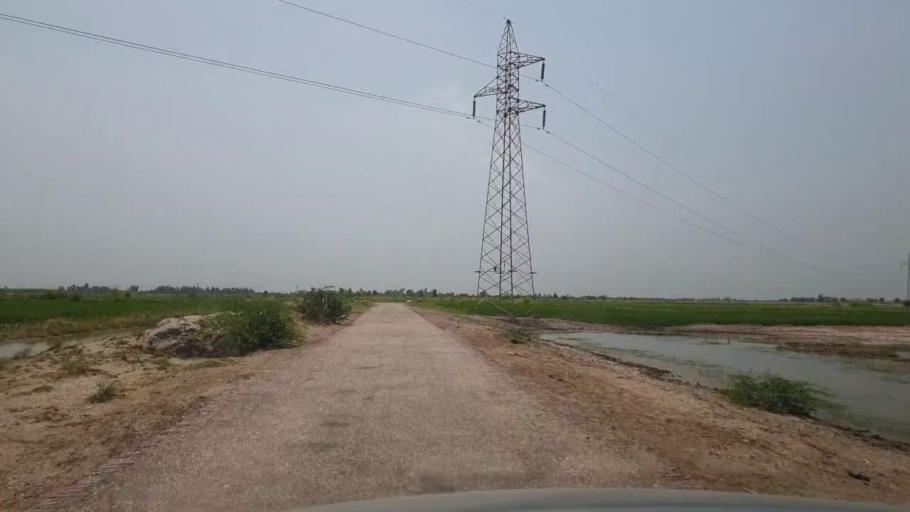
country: PK
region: Sindh
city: Garhi Yasin
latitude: 27.8889
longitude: 68.4944
